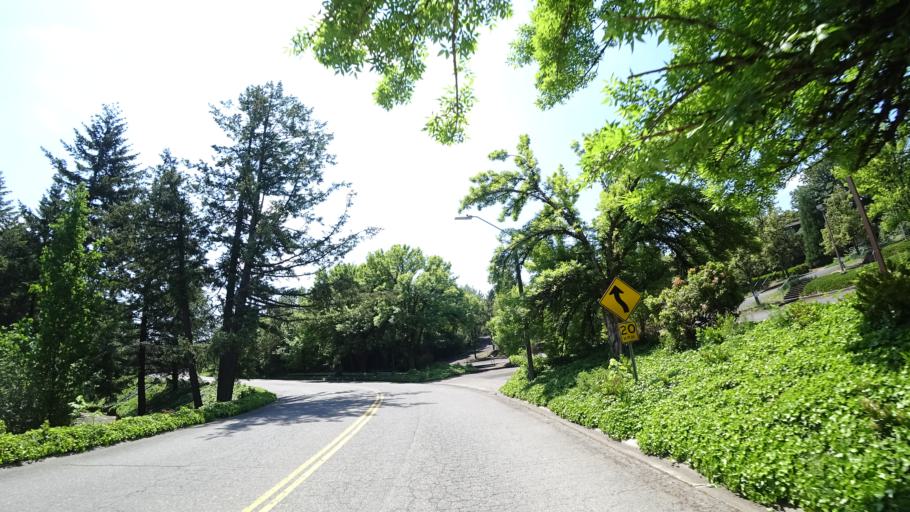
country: US
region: Oregon
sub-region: Washington County
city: Metzger
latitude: 45.4341
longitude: -122.7163
